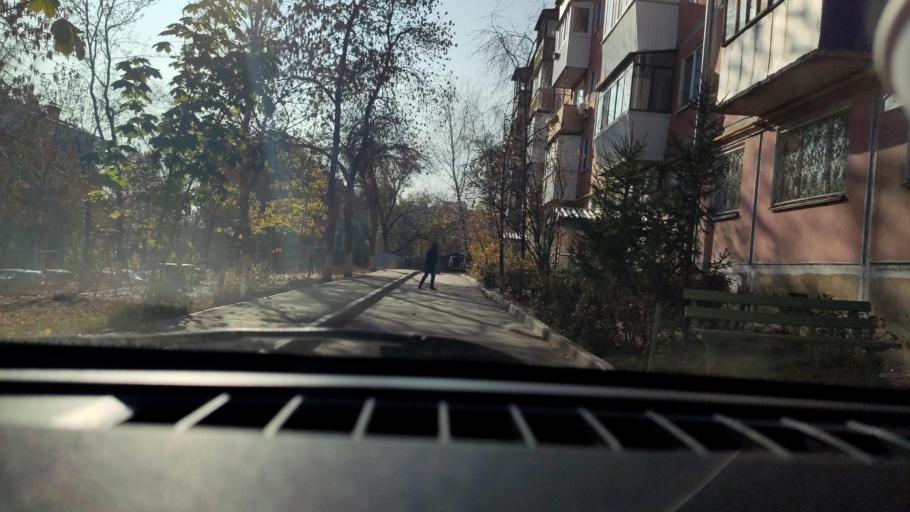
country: RU
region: Samara
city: Samara
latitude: 53.1900
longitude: 50.2075
